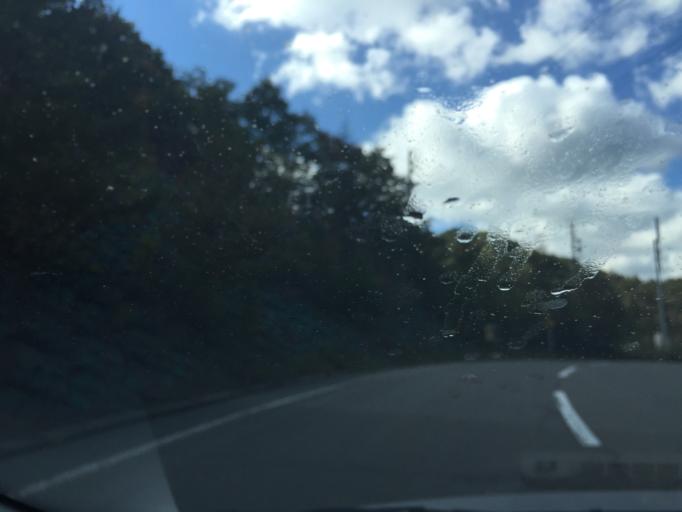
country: JP
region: Gifu
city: Nakatsugawa
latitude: 35.2970
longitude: 137.6708
